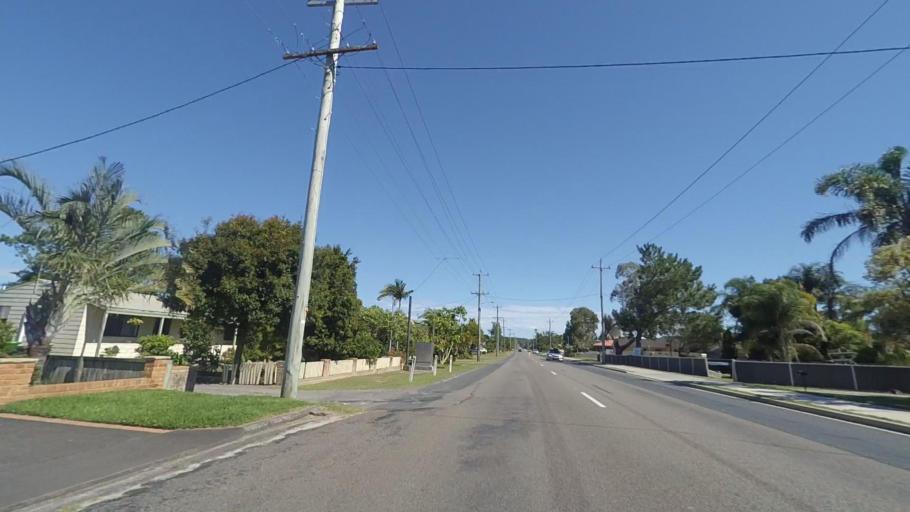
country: AU
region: New South Wales
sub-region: Great Lakes
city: Hawks Nest
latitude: -32.6580
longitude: 152.1511
